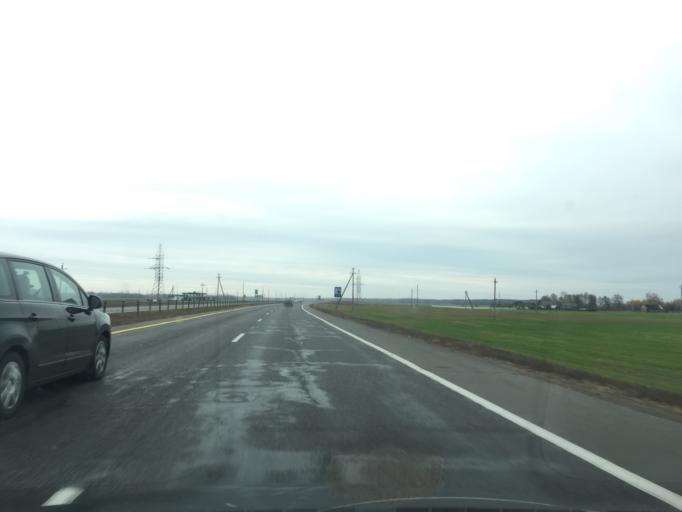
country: BY
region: Gomel
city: Horad Rechytsa
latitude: 52.3350
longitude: 30.5464
